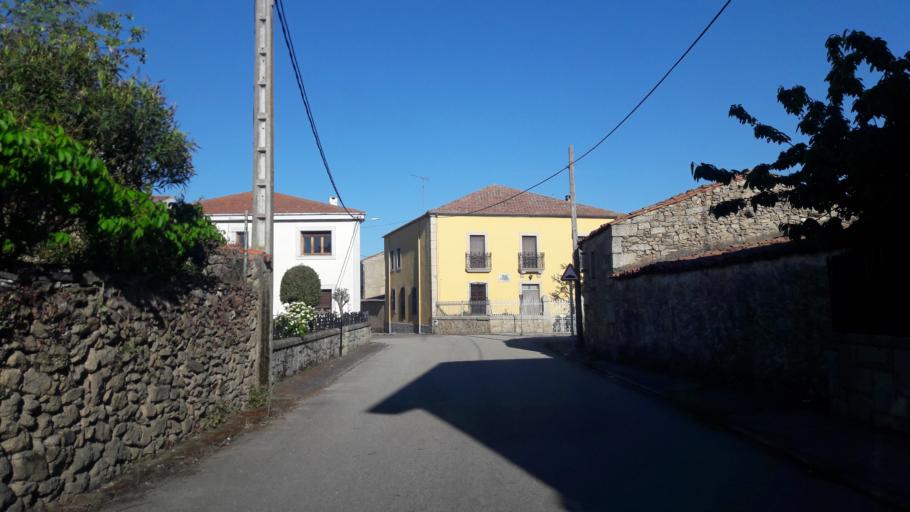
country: ES
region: Castille and Leon
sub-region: Provincia de Salamanca
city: Villavieja de Yeltes
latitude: 40.8769
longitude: -6.4690
